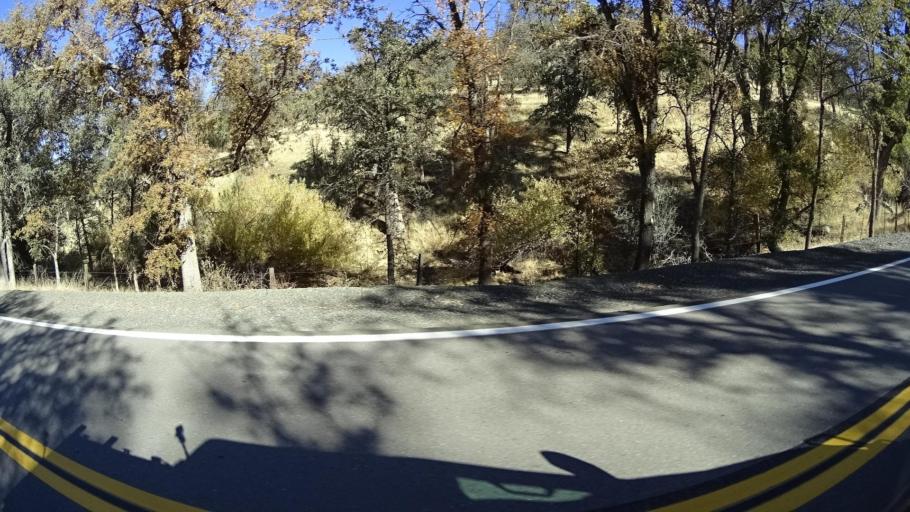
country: US
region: California
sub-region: Kern County
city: Alta Sierra
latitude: 35.7213
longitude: -118.6938
